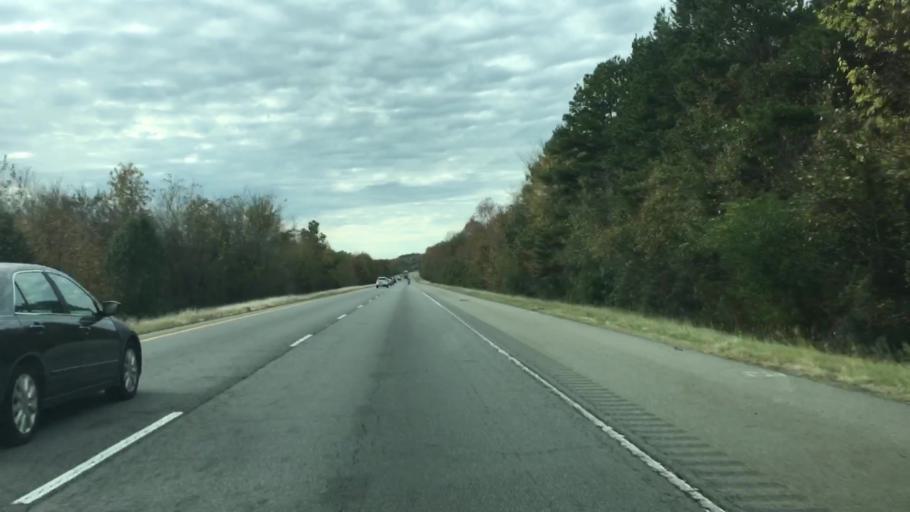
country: US
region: Arkansas
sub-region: Faulkner County
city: Conway
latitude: 35.1203
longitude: -92.4776
